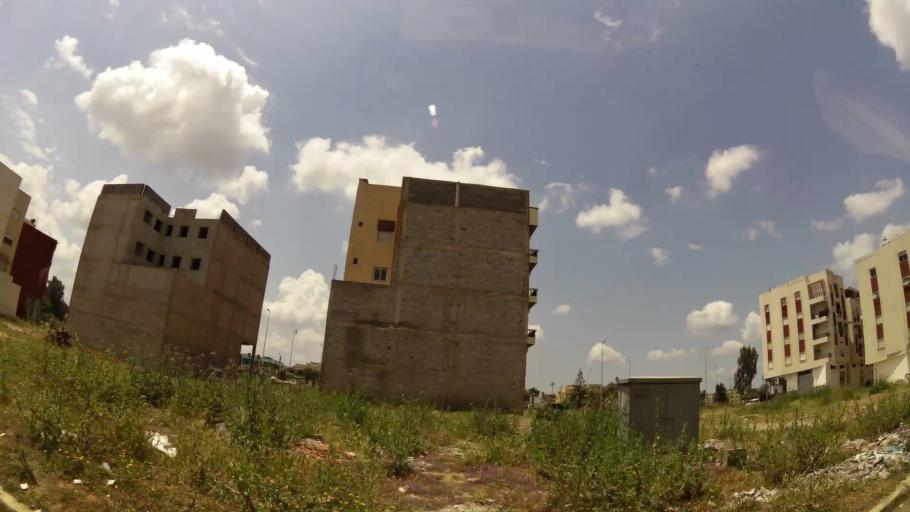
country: MA
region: Rabat-Sale-Zemmour-Zaer
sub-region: Khemisset
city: Tiflet
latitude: 34.0098
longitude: -6.5253
